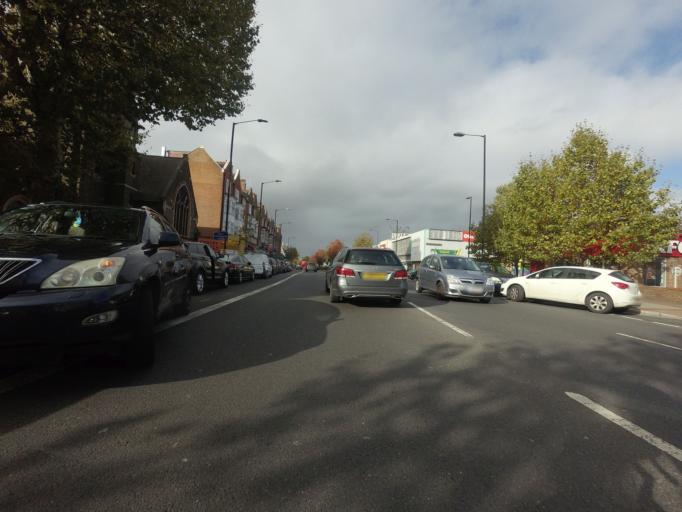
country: GB
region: England
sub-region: Greater London
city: Camberwell
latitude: 51.4821
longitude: -0.0622
